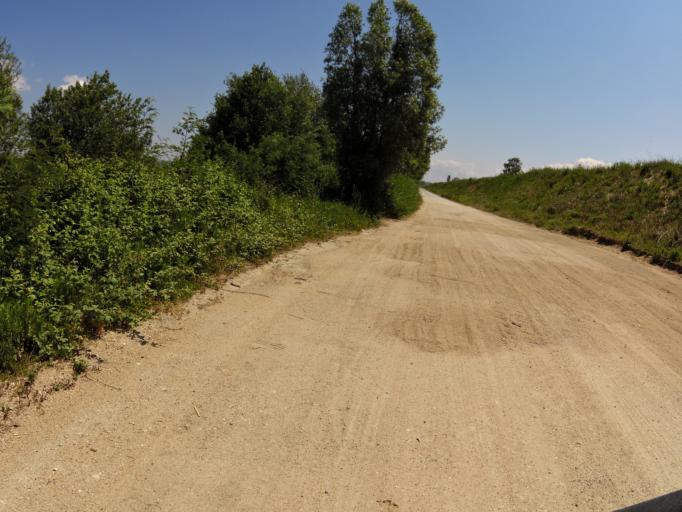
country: PT
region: Coimbra
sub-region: Montemor-O-Velho
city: Montemor-o-Velho
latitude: 40.1484
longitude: -8.7339
